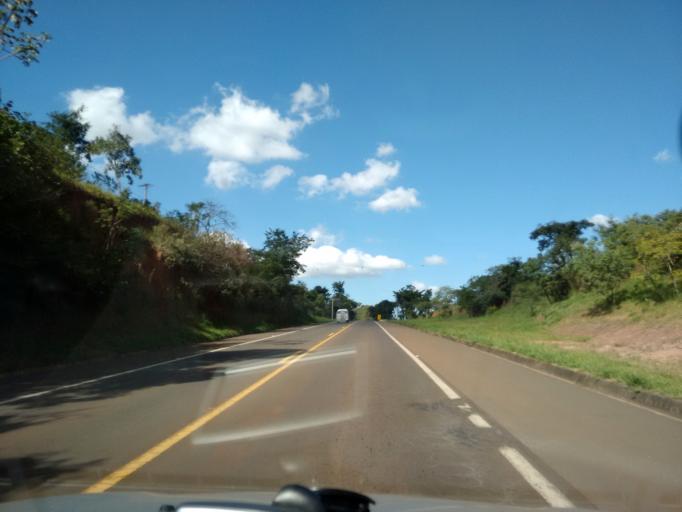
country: BR
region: Sao Paulo
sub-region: Sao Carlos
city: Sao Carlos
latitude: -22.0666
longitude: -47.9098
